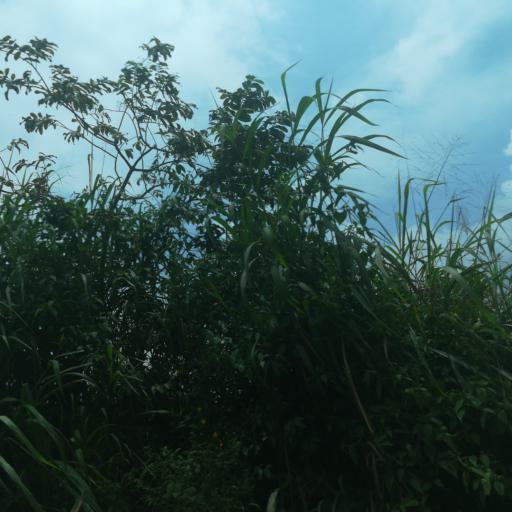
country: NG
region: Lagos
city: Ejirin
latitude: 6.6820
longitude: 3.7990
